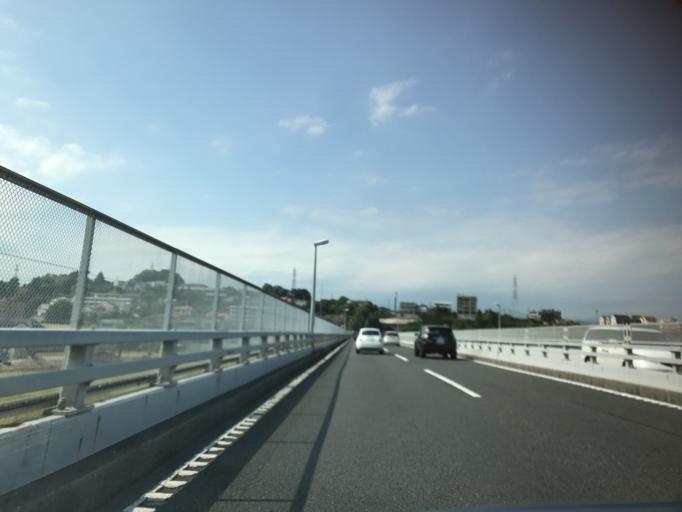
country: JP
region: Kanagawa
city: Odawara
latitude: 35.2710
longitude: 139.1504
